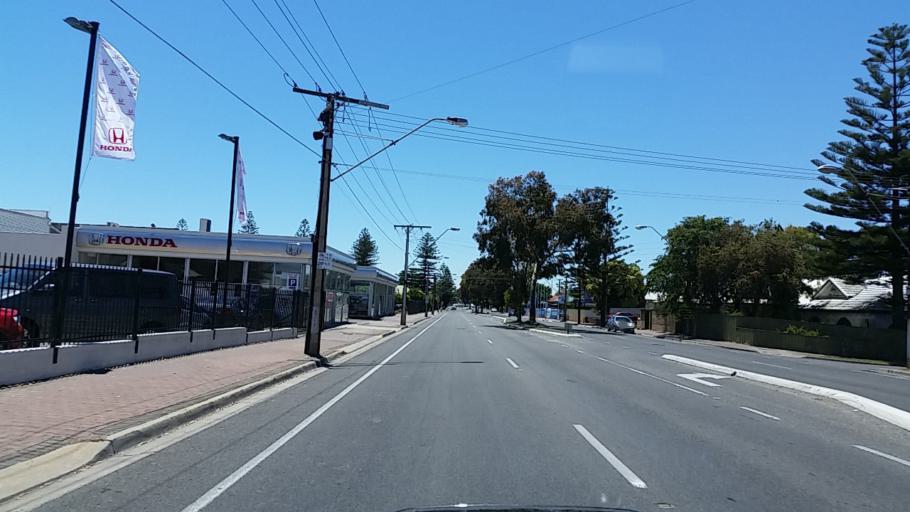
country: AU
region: South Australia
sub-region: Adelaide
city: Glenelg
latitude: -34.9901
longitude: 138.5209
